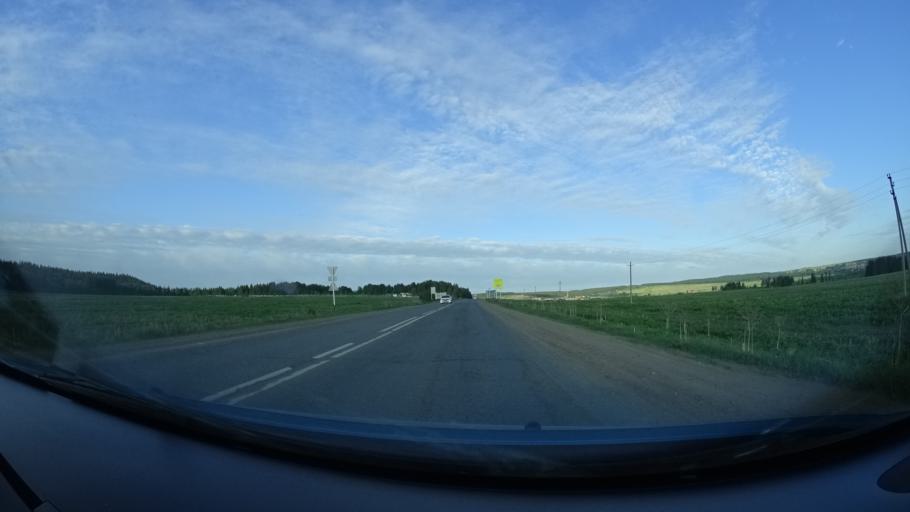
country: RU
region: Perm
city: Kultayevo
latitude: 57.8619
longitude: 55.8743
